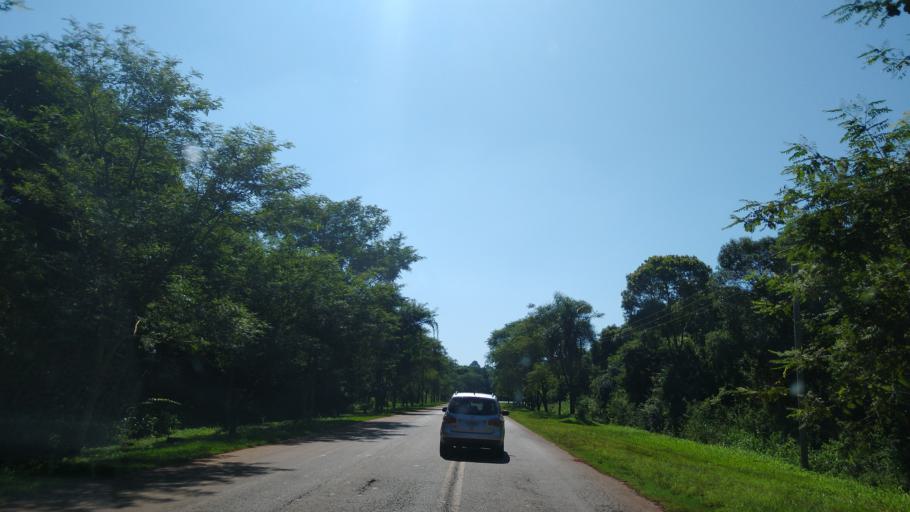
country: AR
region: Misiones
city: Puerto Esperanza
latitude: -26.0201
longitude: -54.5948
